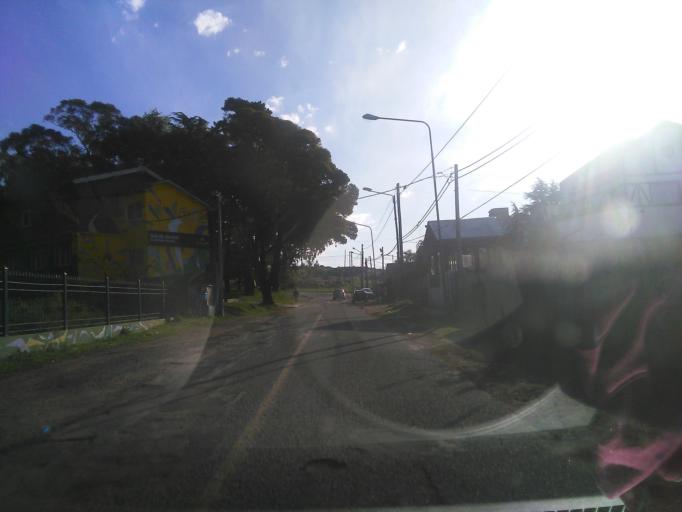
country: AR
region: Buenos Aires
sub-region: Partido de Tandil
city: Tandil
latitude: -37.3393
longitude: -59.1397
